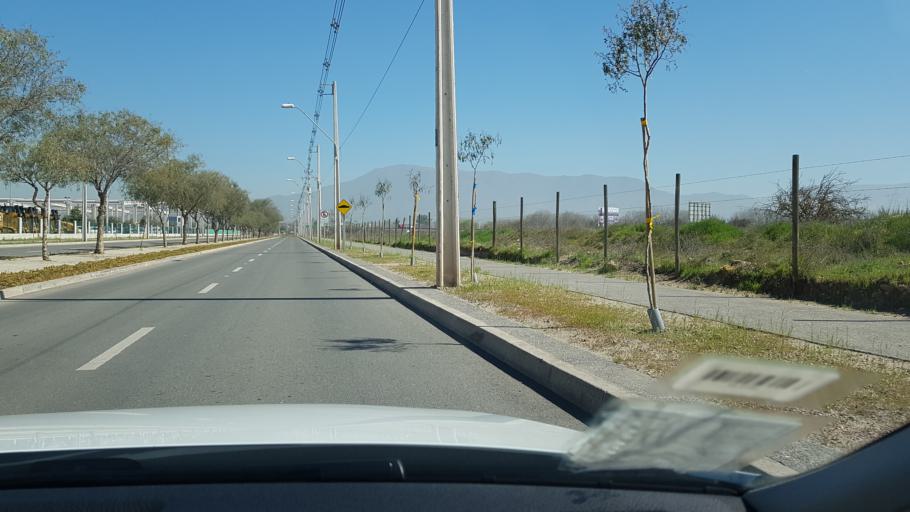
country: CL
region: Santiago Metropolitan
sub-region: Provincia de Santiago
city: Lo Prado
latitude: -33.4262
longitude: -70.7956
